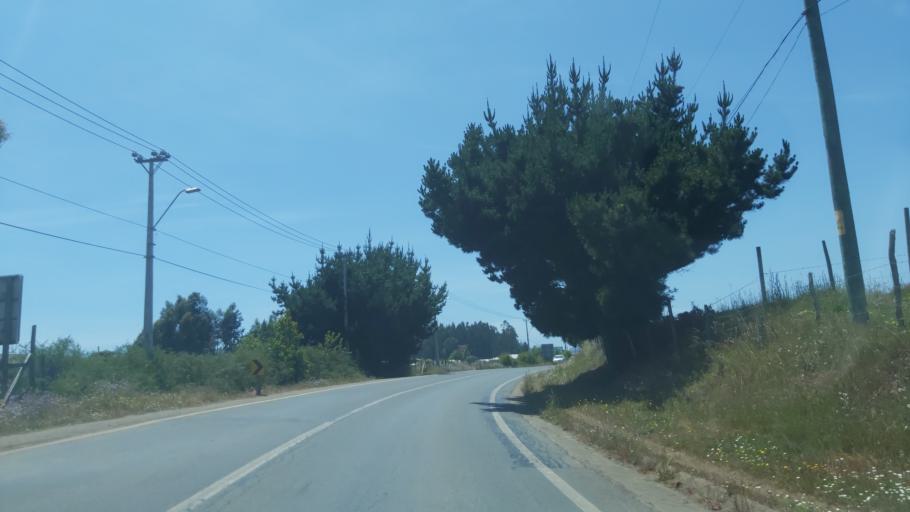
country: CL
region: Maule
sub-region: Provincia de Cauquenes
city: Cauquenes
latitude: -35.7996
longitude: -72.5636
